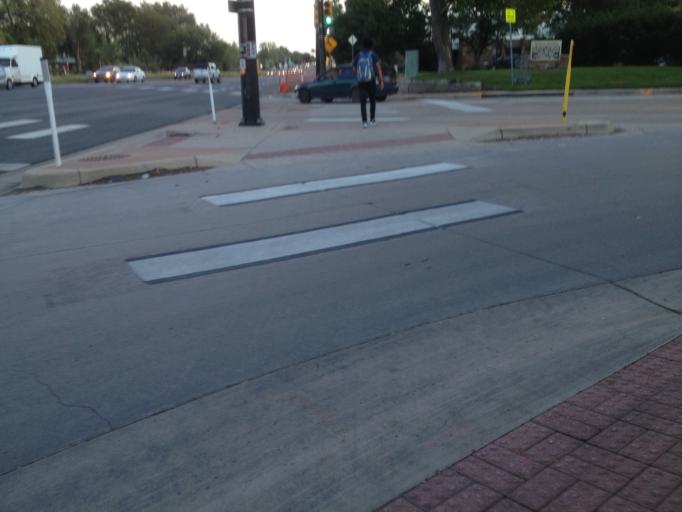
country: US
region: Colorado
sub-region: Boulder County
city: Boulder
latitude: 39.9824
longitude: -105.2474
